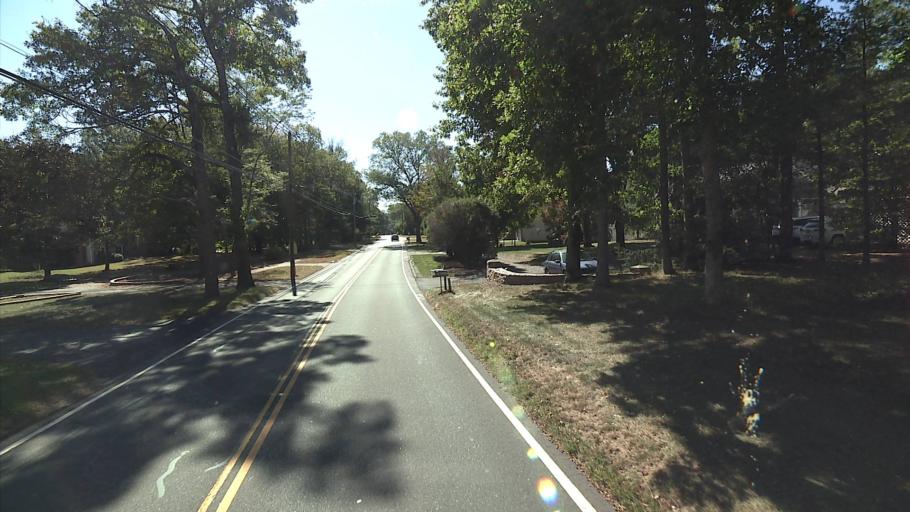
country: US
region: Connecticut
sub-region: Hartford County
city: Glastonbury Center
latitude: 41.7026
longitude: -72.5313
